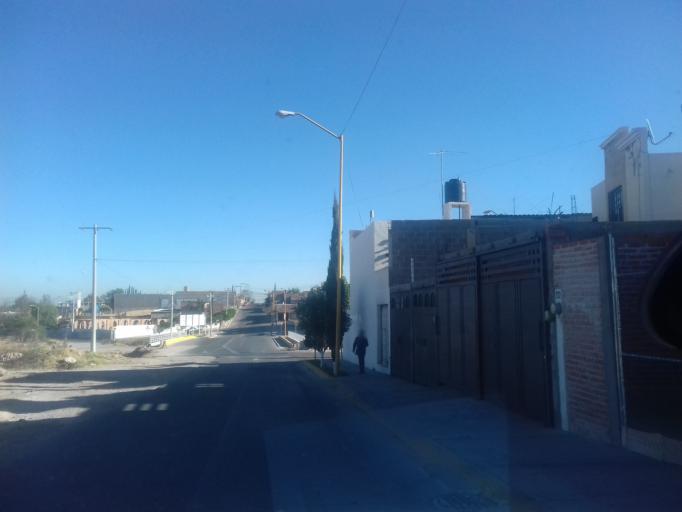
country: MX
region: Aguascalientes
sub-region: Aguascalientes
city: San Sebastian [Fraccionamiento]
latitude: 21.8477
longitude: -102.2637
